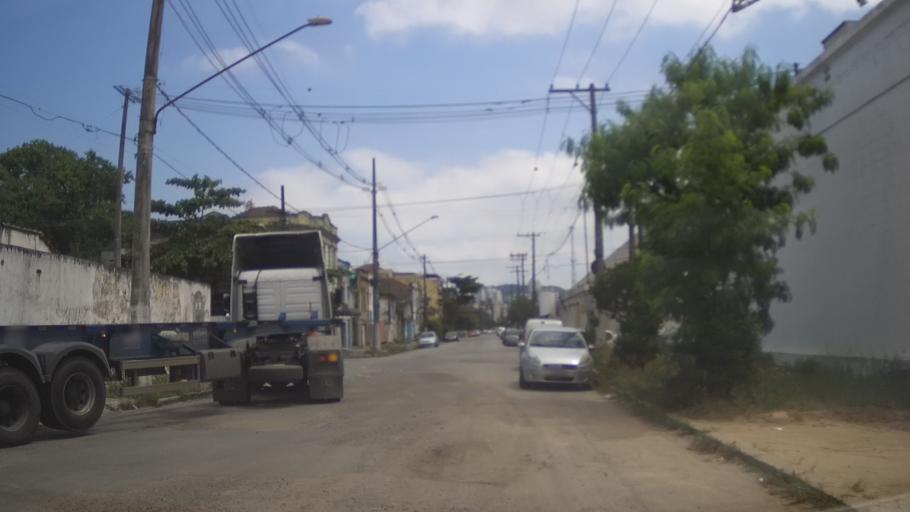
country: BR
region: Sao Paulo
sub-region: Santos
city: Santos
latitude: -23.9526
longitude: -46.3137
